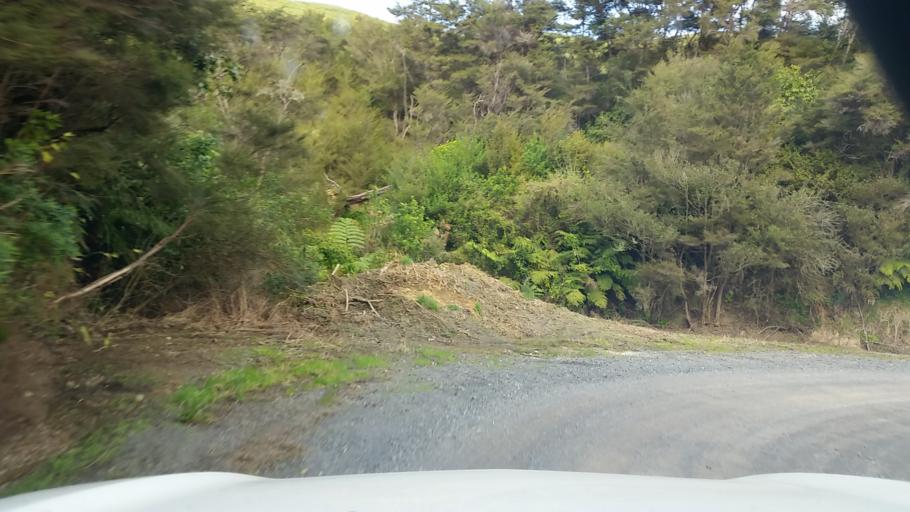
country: NZ
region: Waikato
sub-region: Hauraki District
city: Ngatea
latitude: -37.4827
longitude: 175.4521
